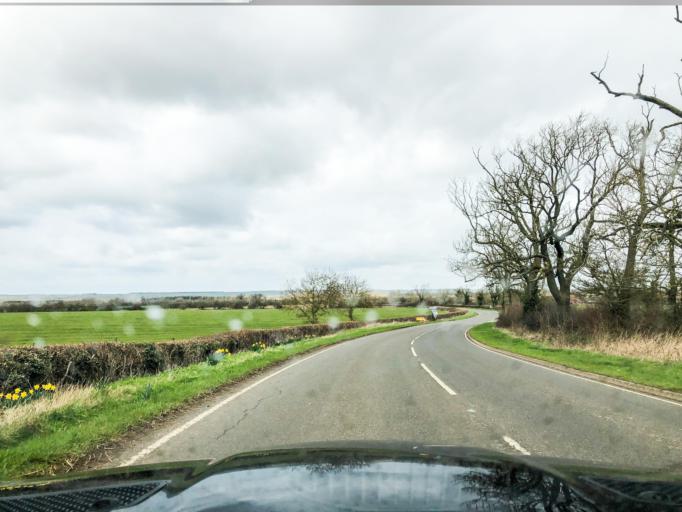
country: GB
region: England
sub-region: Oxfordshire
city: Hanwell
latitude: 52.1377
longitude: -1.4503
